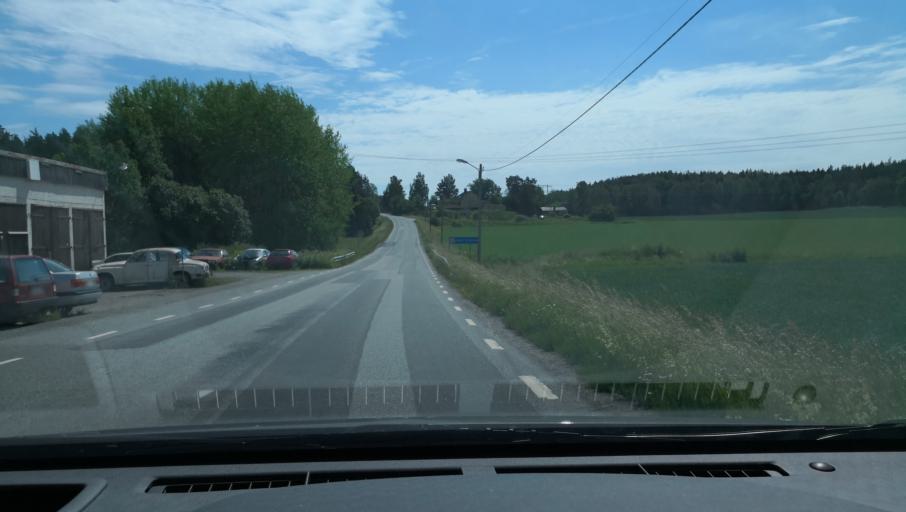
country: SE
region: Uppsala
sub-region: Habo Kommun
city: Balsta
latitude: 59.6625
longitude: 17.4496
